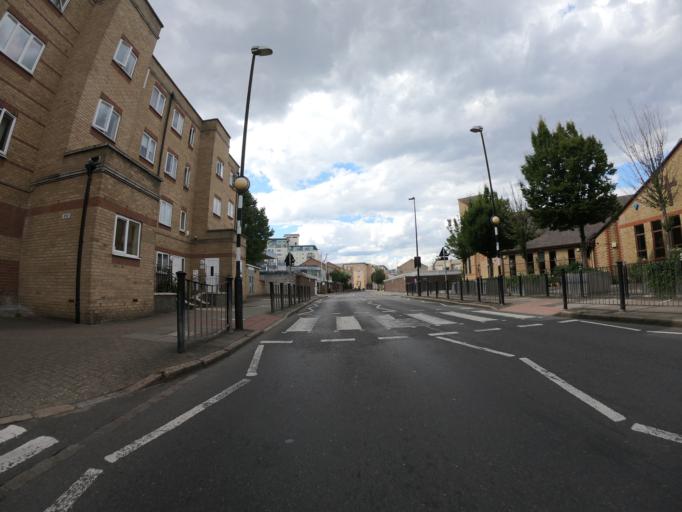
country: GB
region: England
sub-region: Greater London
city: Poplar
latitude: 51.4907
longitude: -0.0233
